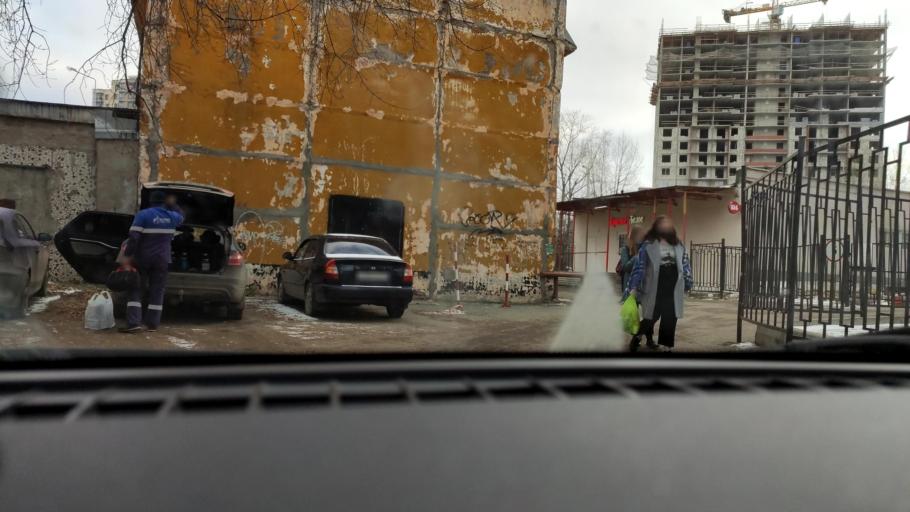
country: RU
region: Perm
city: Perm
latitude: 57.9813
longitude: 56.2139
